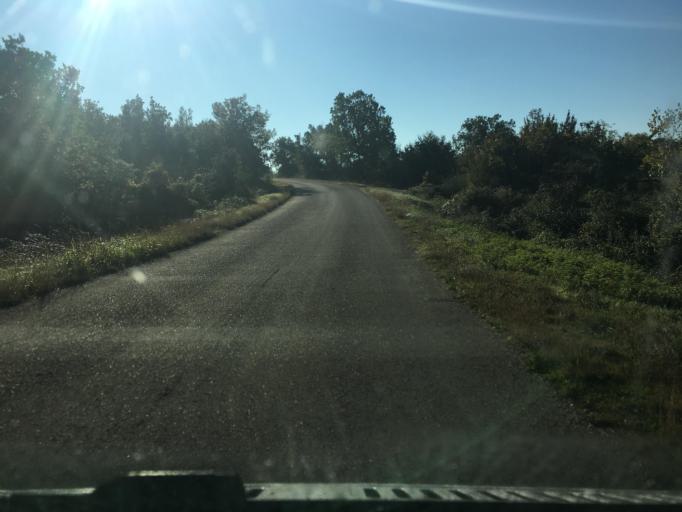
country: FR
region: Languedoc-Roussillon
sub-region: Departement du Gard
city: Barjac
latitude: 44.1775
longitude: 4.3391
